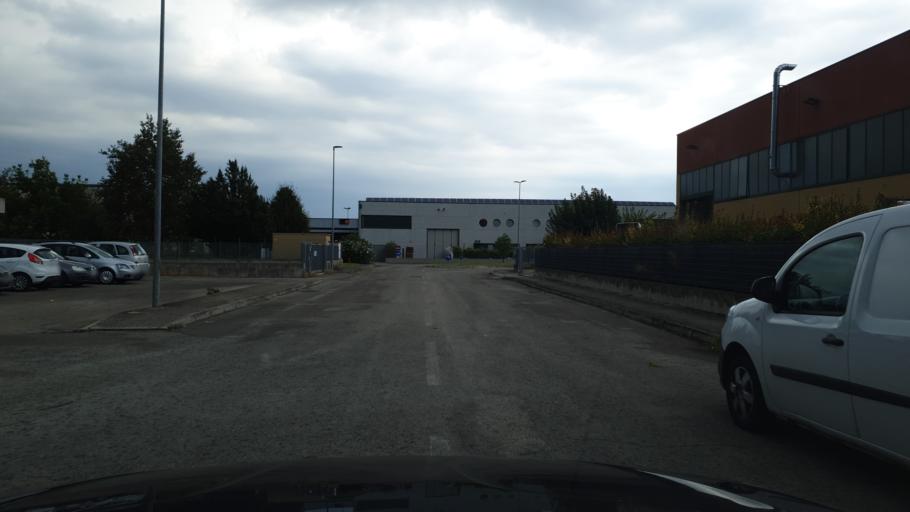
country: IT
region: Veneto
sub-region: Provincia di Vicenza
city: Noventa Vicentina
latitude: 45.3052
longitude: 11.5620
